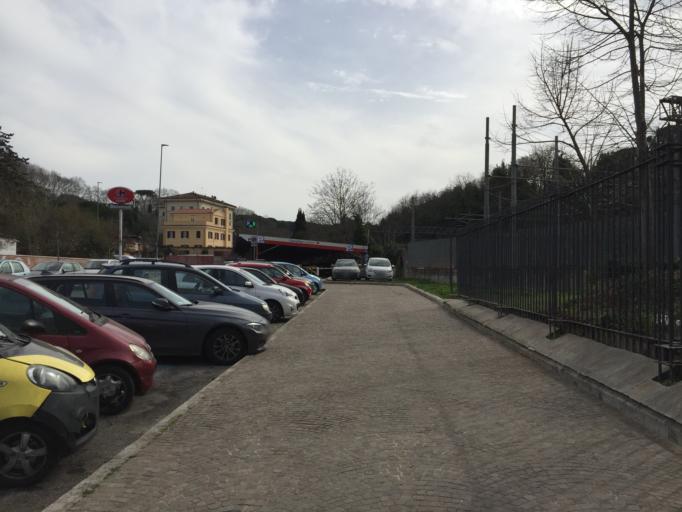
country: VA
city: Vatican City
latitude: 41.8951
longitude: 12.4562
